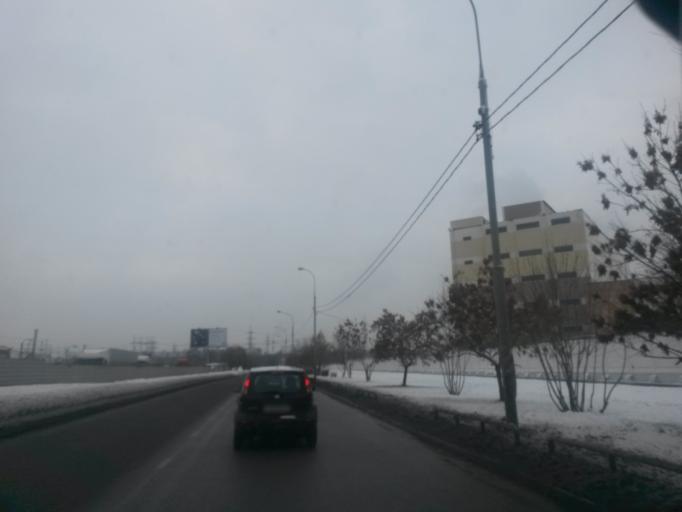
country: RU
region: Moscow
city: Mikhalkovo
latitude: 55.6729
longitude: 37.4343
